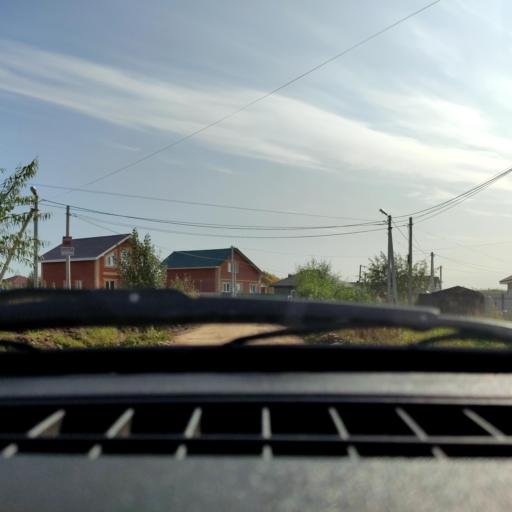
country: RU
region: Bashkortostan
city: Ufa
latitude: 54.6570
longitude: 56.0747
